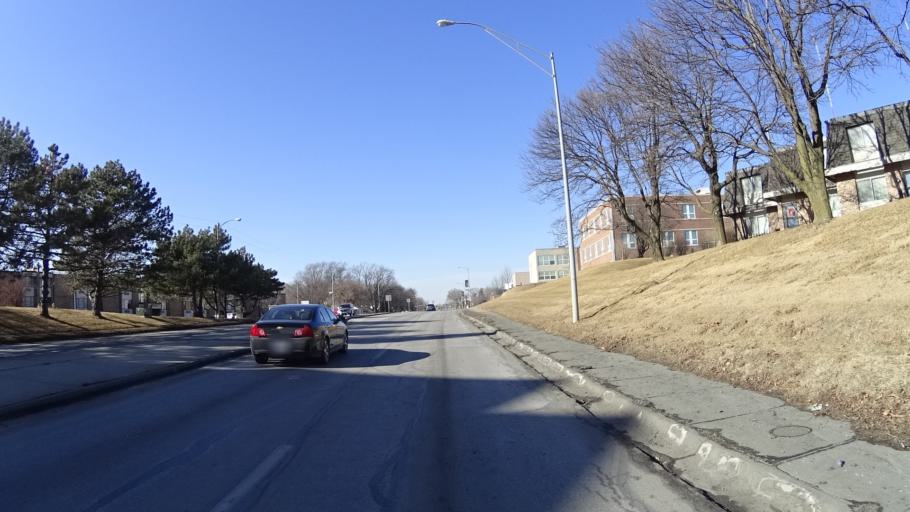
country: US
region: Nebraska
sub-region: Douglas County
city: Ralston
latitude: 41.2991
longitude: -96.0264
